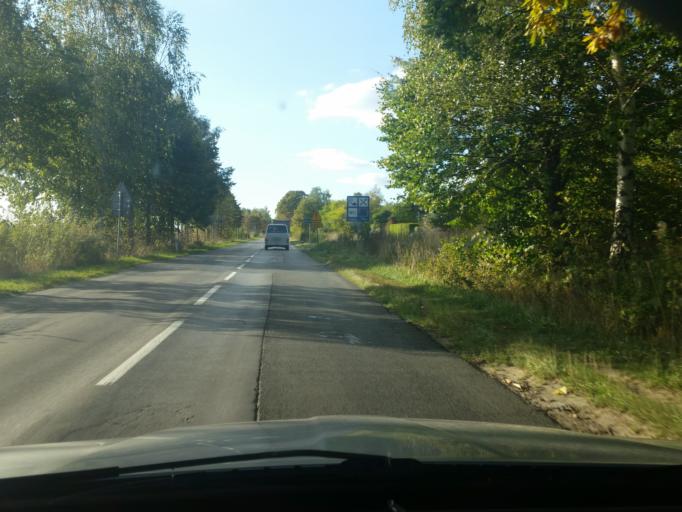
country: PL
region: Pomeranian Voivodeship
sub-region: Powiat chojnicki
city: Chojnice
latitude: 53.7146
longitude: 17.5266
